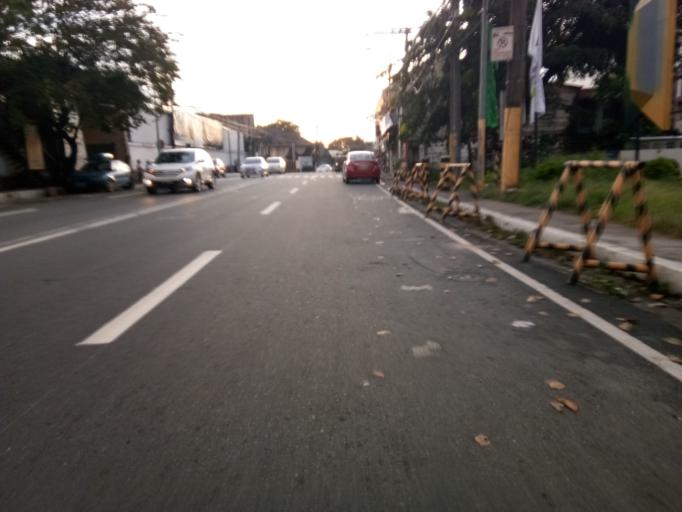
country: PH
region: Metro Manila
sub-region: San Juan
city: San Juan
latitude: 14.6089
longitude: 121.0466
